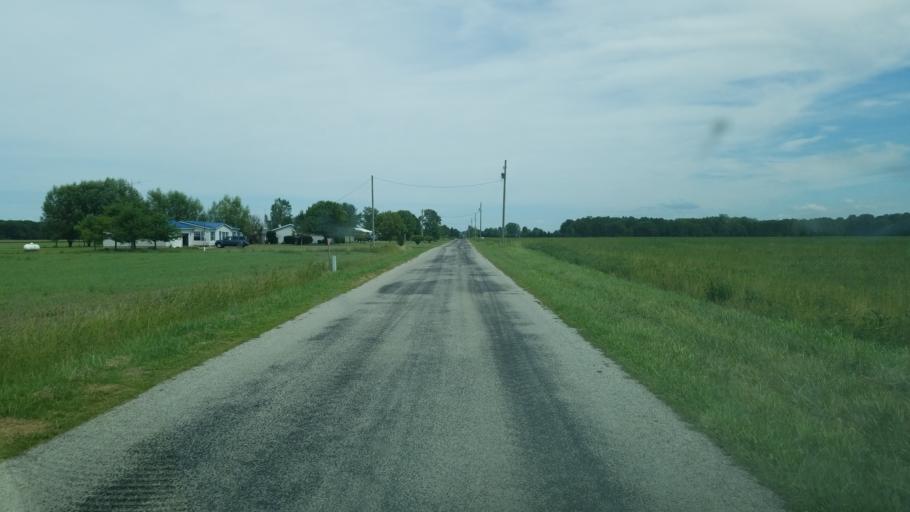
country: US
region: Ohio
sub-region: Union County
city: Richwood
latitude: 40.5932
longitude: -83.3032
